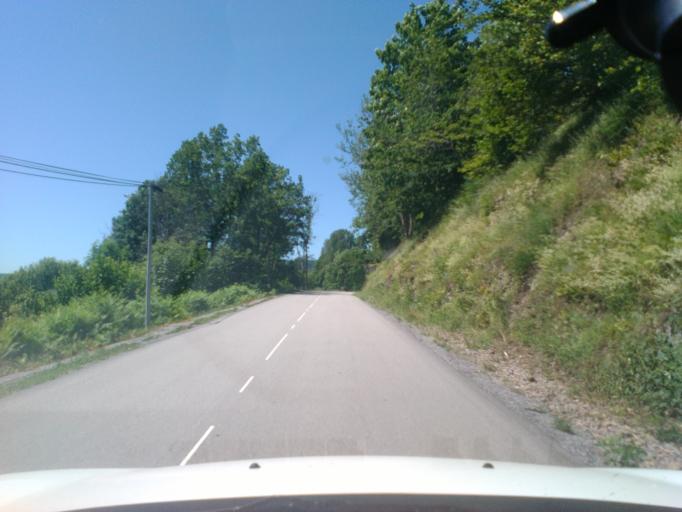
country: FR
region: Lorraine
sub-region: Departement des Vosges
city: La Bresse
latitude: 48.0006
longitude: 6.8558
